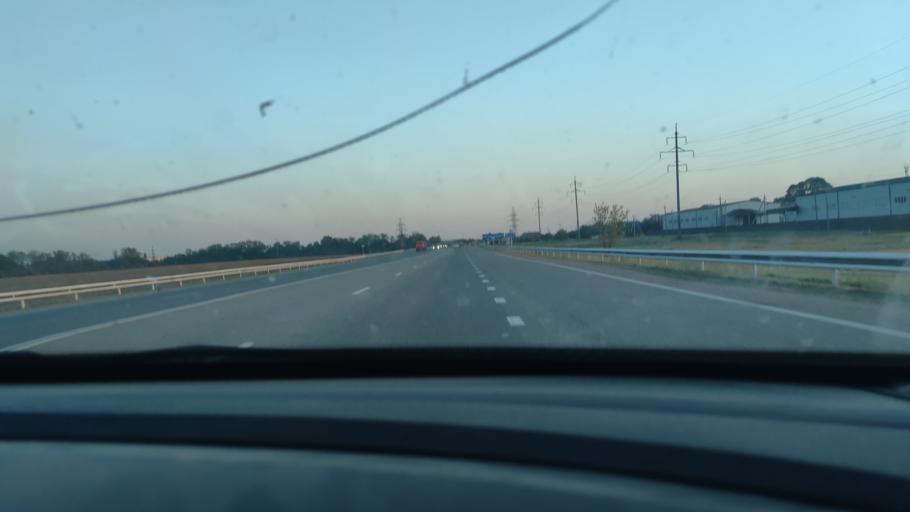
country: RU
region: Krasnodarskiy
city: Timashevsk
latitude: 45.6160
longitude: 38.9867
